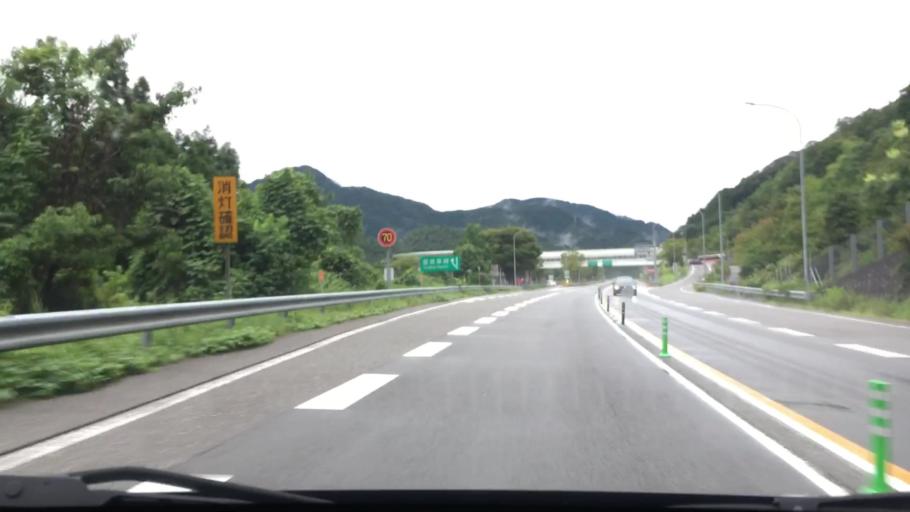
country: JP
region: Hyogo
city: Nishiwaki
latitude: 35.2154
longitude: 134.7935
